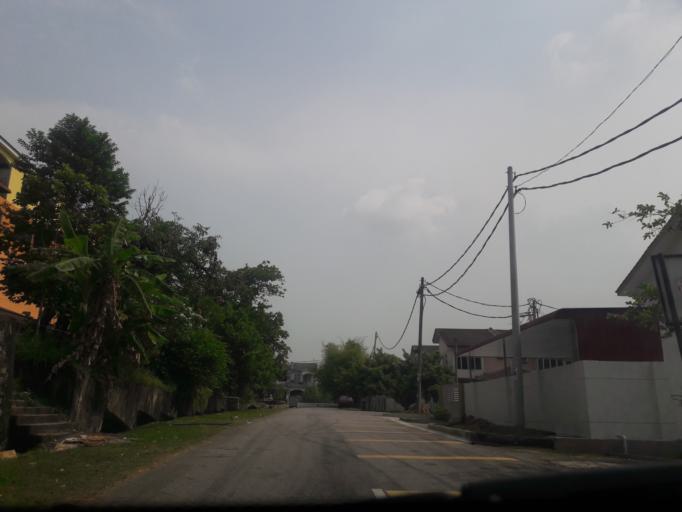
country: MY
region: Kedah
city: Kulim
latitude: 5.3638
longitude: 100.5378
